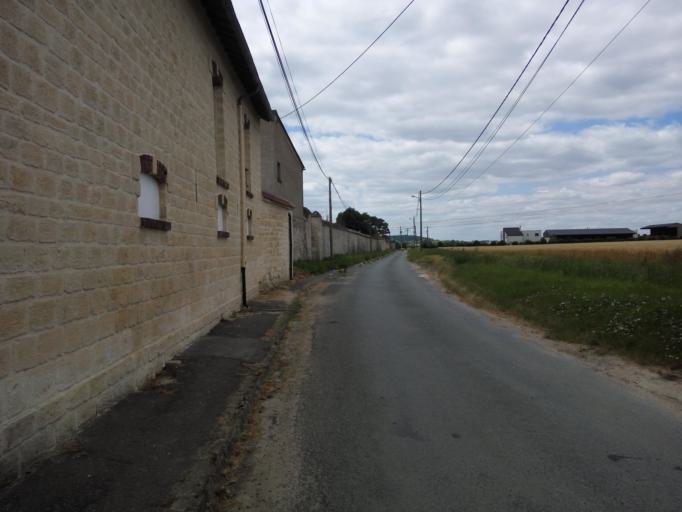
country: FR
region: Picardie
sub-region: Departement de l'Oise
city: Boran-sur-Oise
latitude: 49.1614
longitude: 2.3531
